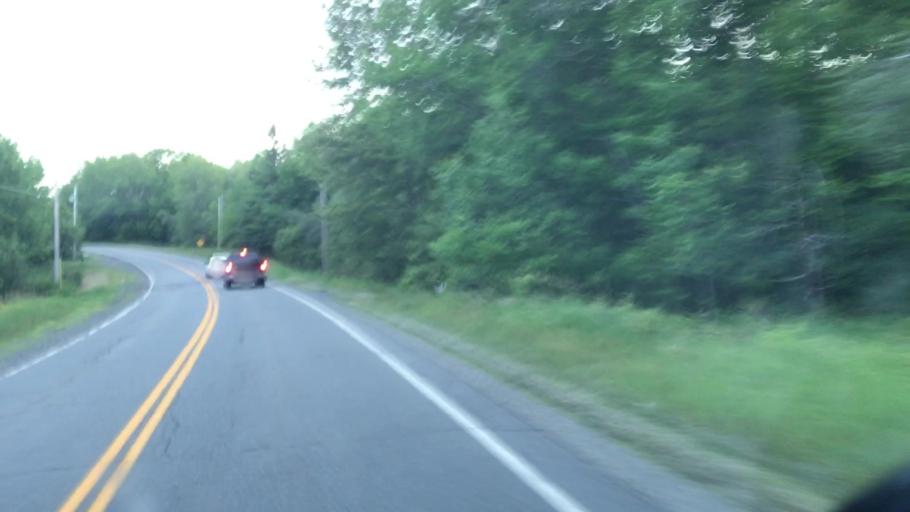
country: US
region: Maine
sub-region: Penobscot County
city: Medway
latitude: 45.6178
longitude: -68.3018
